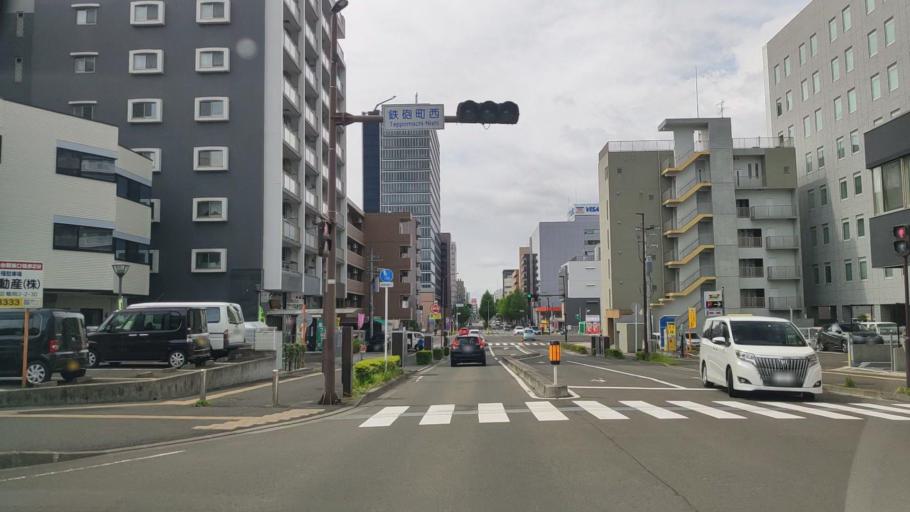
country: JP
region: Miyagi
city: Sendai-shi
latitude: 38.2638
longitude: 140.8869
